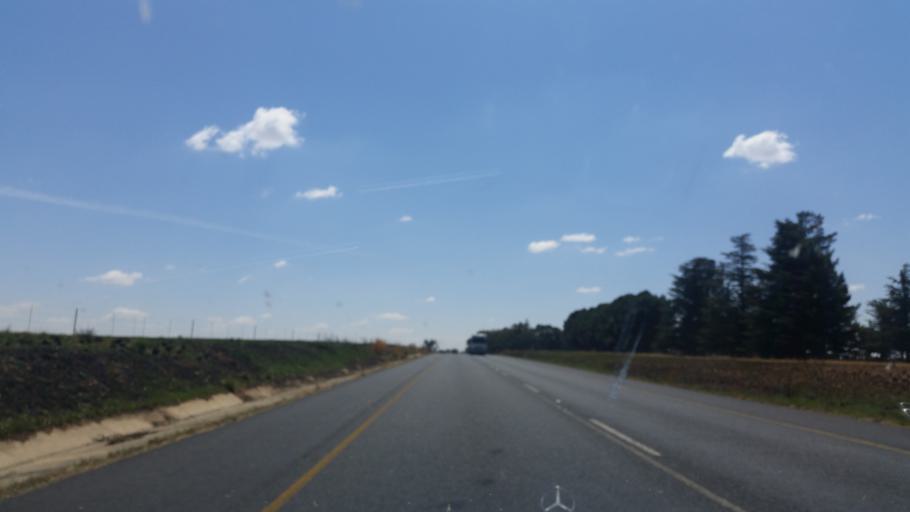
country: ZA
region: Orange Free State
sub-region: Thabo Mofutsanyana District Municipality
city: Reitz
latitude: -28.0967
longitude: 28.6565
